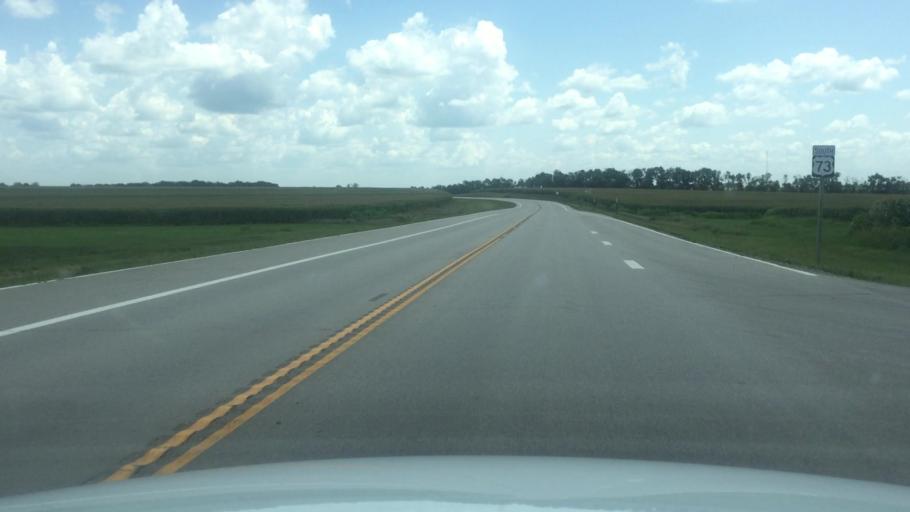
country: US
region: Kansas
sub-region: Brown County
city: Horton
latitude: 39.6637
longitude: -95.4150
